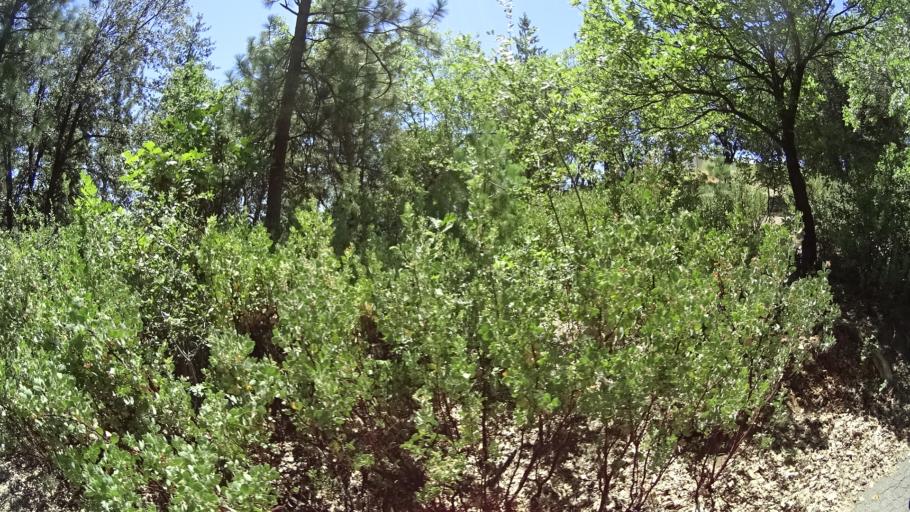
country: US
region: California
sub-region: Calaveras County
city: Mountain Ranch
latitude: 38.2530
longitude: -120.5303
